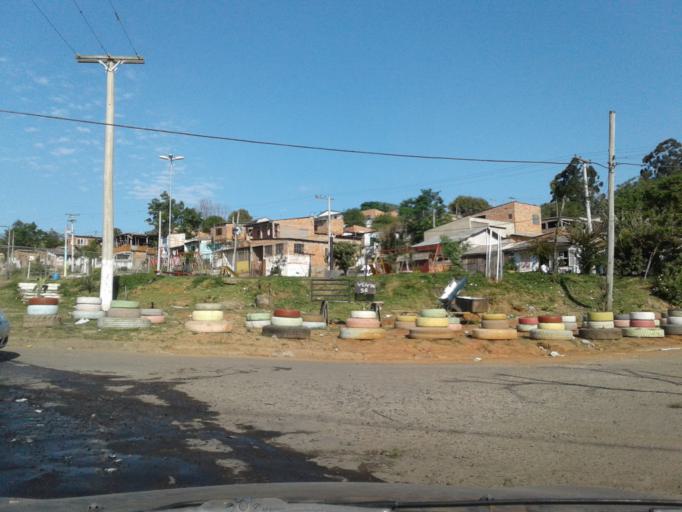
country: BR
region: Rio Grande do Sul
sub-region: Porto Alegre
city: Porto Alegre
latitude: -30.0492
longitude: -51.1568
